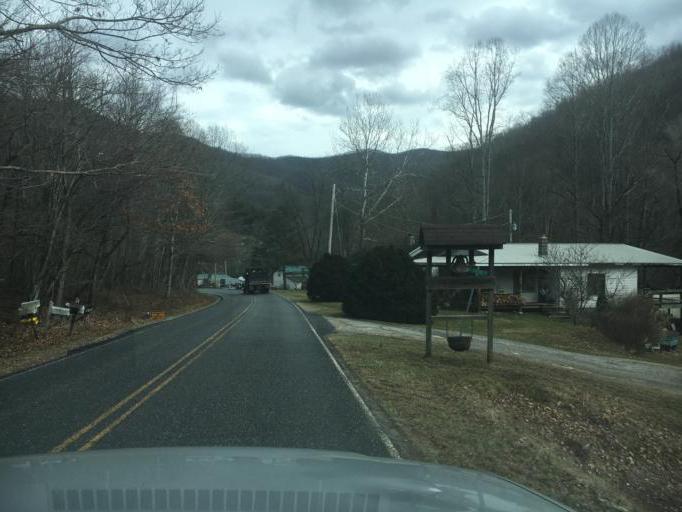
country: US
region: North Carolina
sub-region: Haywood County
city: Canton
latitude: 35.4008
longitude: -82.8126
